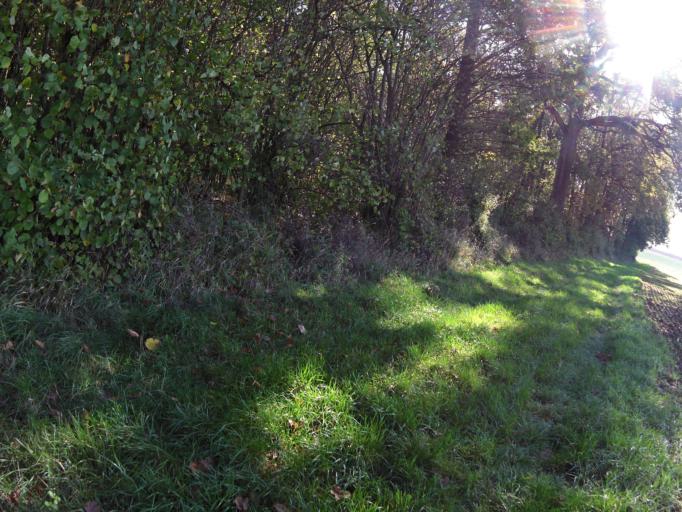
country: DE
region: Bavaria
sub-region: Regierungsbezirk Unterfranken
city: Sulzfeld am Main
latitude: 49.7126
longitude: 10.0939
